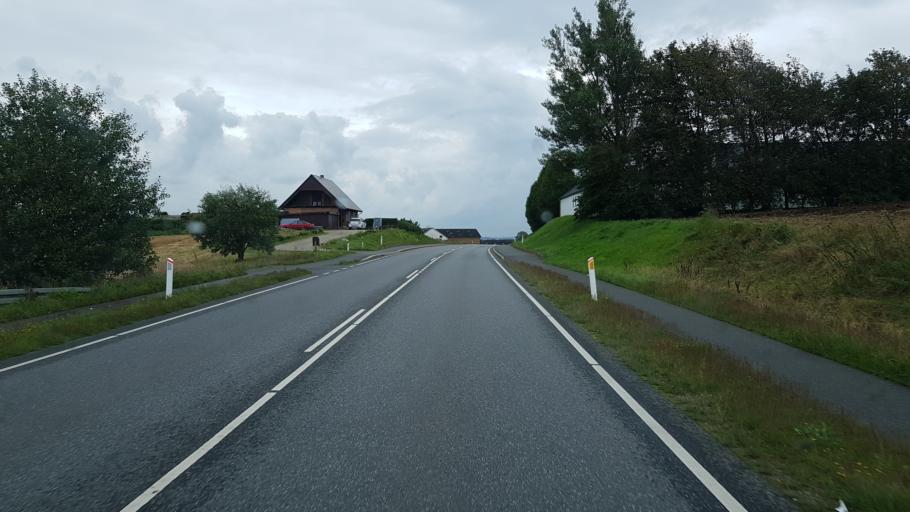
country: DK
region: Central Jutland
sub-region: Horsens Kommune
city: Braedstrup
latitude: 55.9119
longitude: 9.7145
